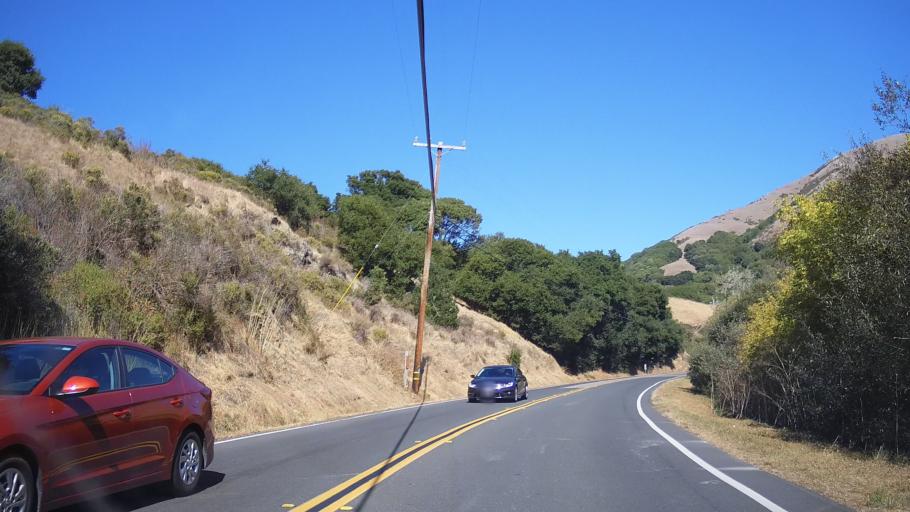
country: US
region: California
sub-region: Marin County
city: Inverness
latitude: 38.0826
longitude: -122.7833
